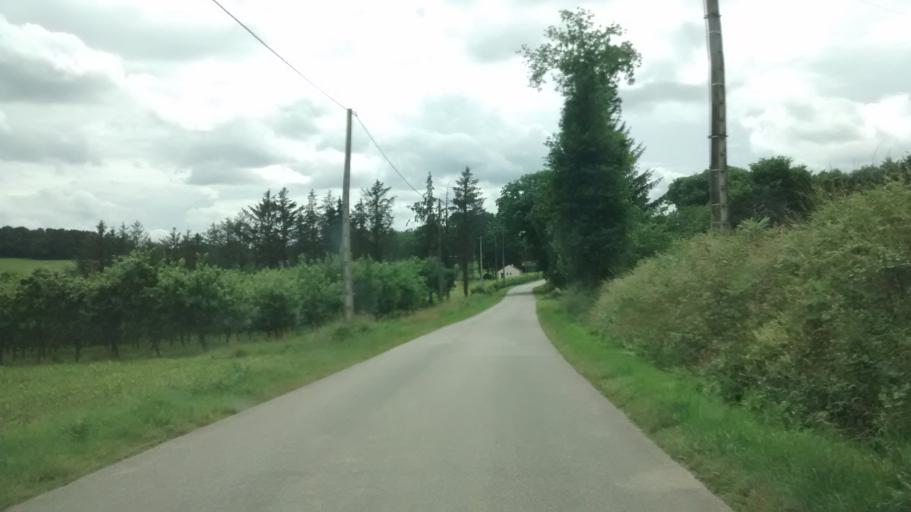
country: FR
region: Brittany
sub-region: Departement du Morbihan
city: Ruffiac
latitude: 47.8416
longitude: -2.2145
